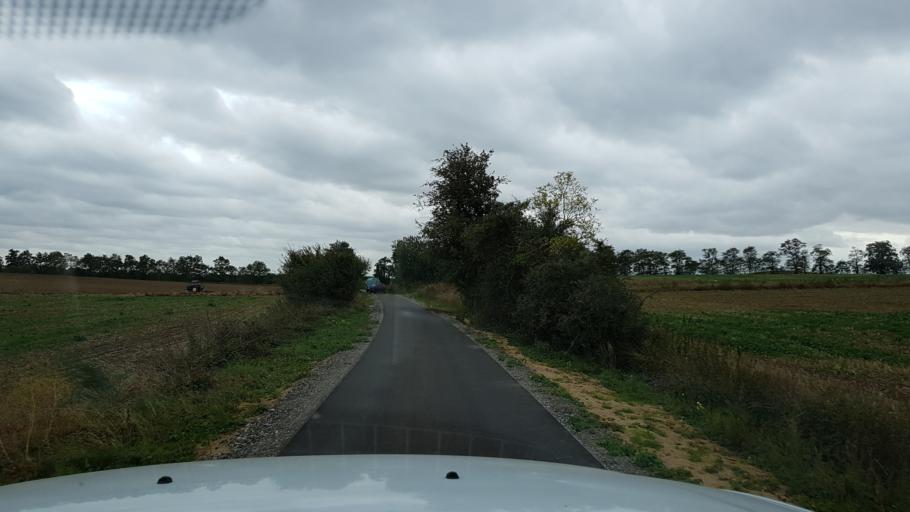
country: PL
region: West Pomeranian Voivodeship
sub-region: Powiat gryfinski
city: Cedynia
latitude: 52.8598
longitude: 14.2840
